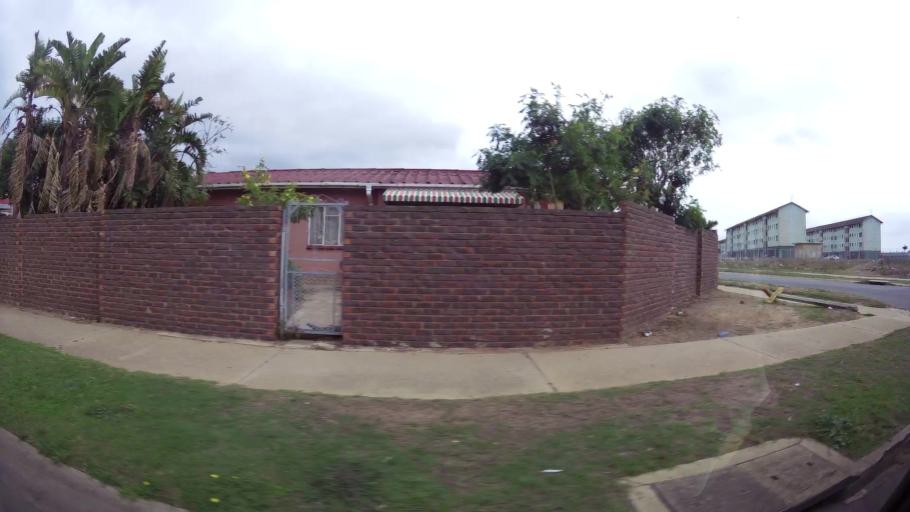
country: ZA
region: Eastern Cape
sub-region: Nelson Mandela Bay Metropolitan Municipality
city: Port Elizabeth
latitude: -33.8959
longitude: 25.5614
